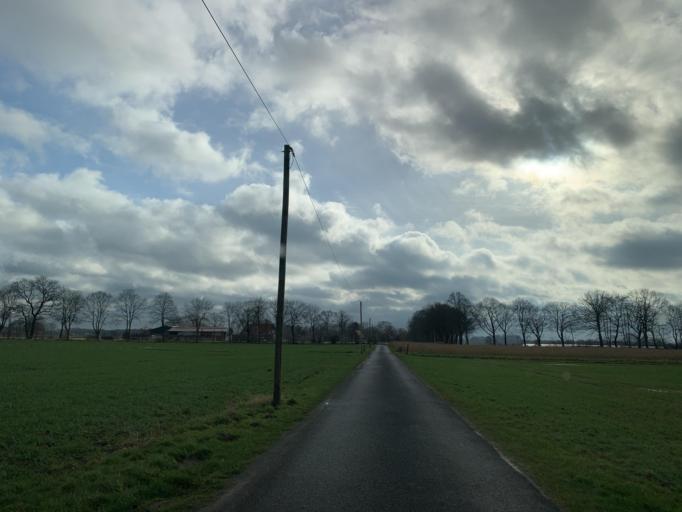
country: DE
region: North Rhine-Westphalia
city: Ludinghausen
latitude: 51.7854
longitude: 7.4742
